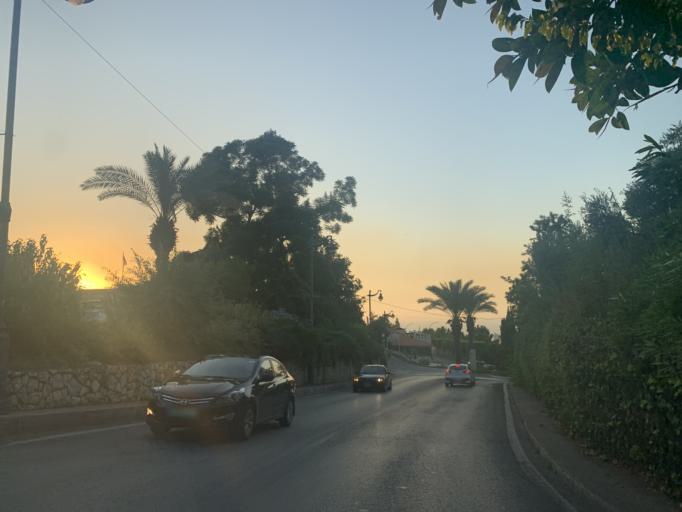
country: LB
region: Mont-Liban
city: Djounie
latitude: 33.9665
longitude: 35.6258
